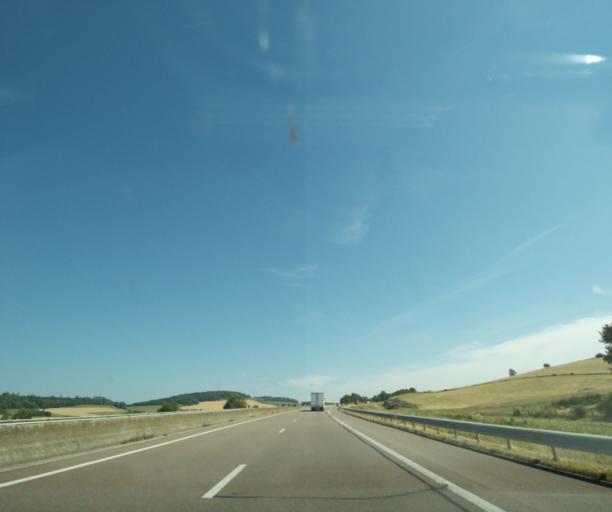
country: FR
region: Lorraine
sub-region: Departement des Vosges
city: Chatenois
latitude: 48.3622
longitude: 5.8668
